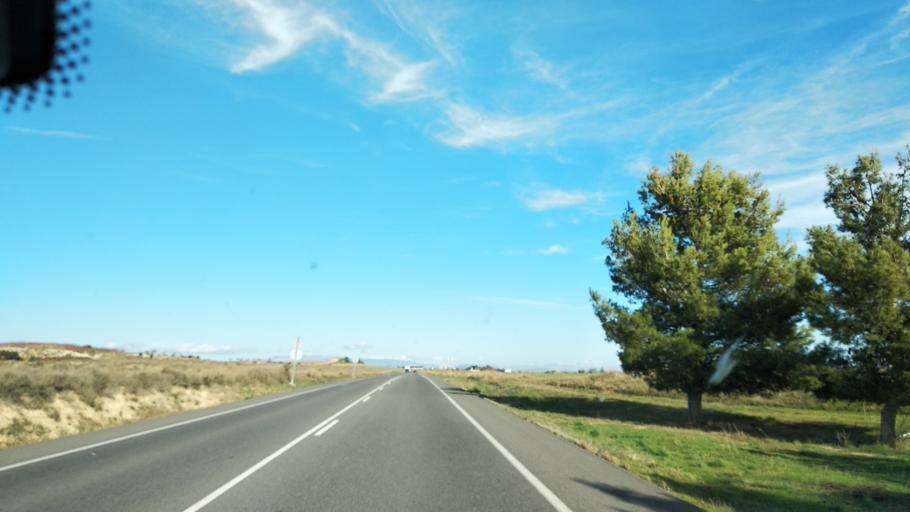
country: ES
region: Catalonia
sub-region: Provincia de Lleida
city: Corbins
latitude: 41.6726
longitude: 0.6708
